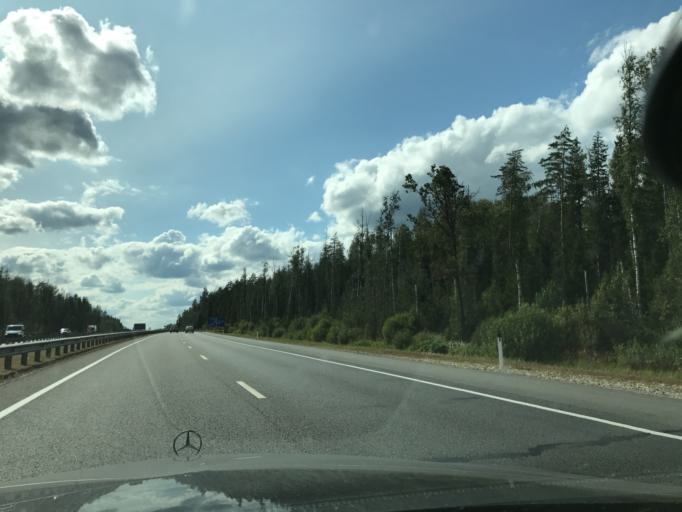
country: RU
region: Vladimir
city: Sudogda
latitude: 56.1408
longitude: 40.8990
